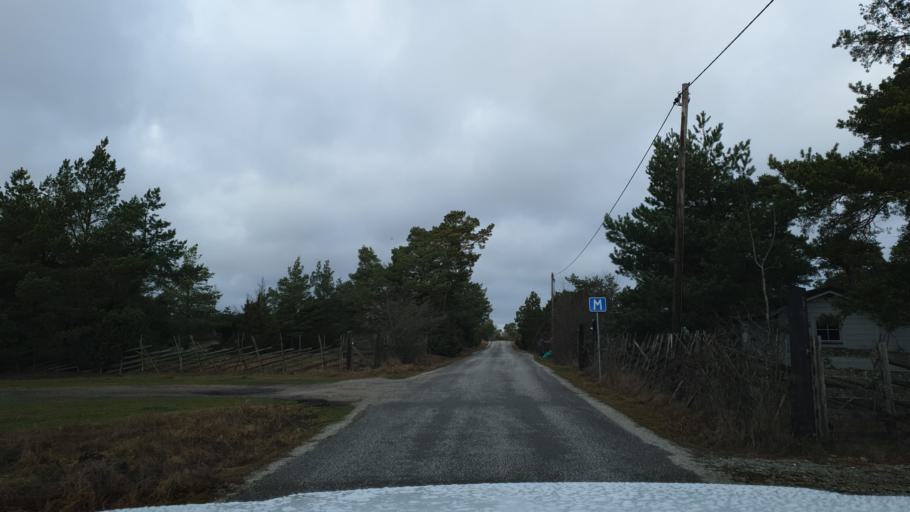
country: SE
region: Gotland
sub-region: Gotland
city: Slite
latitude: 57.3868
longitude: 18.8085
